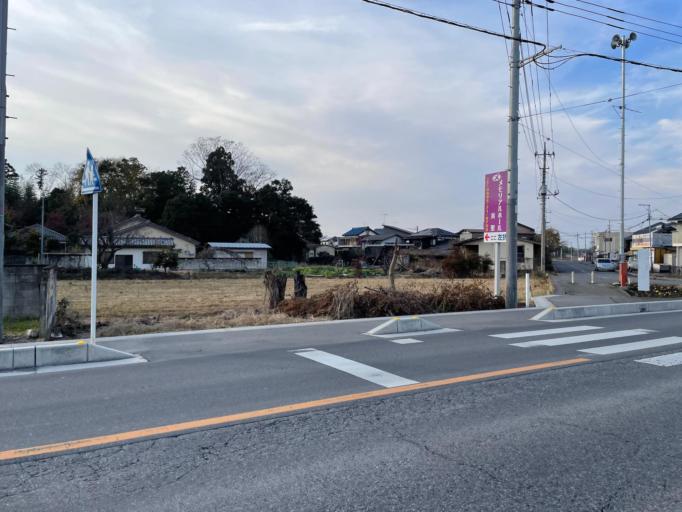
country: JP
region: Saitama
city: Kodamacho-kodamaminami
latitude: 36.1718
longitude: 139.1831
